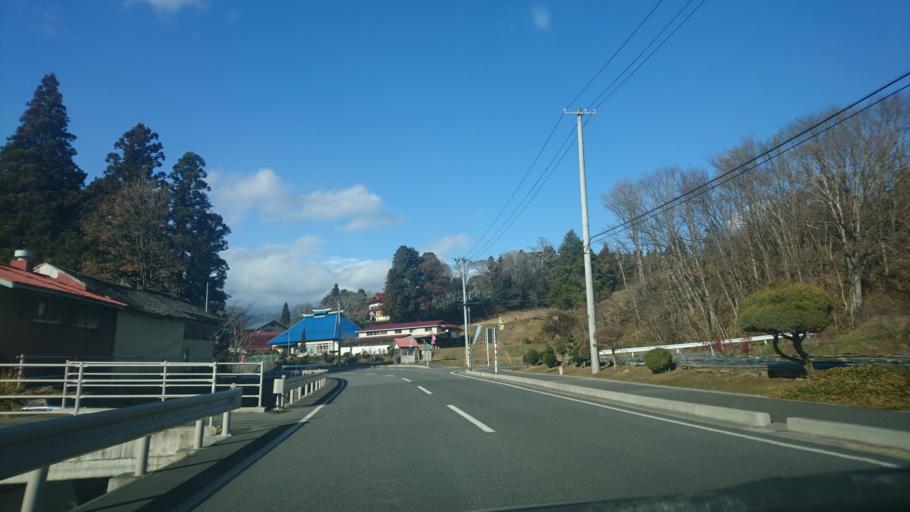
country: JP
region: Iwate
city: Mizusawa
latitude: 39.0419
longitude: 141.3729
